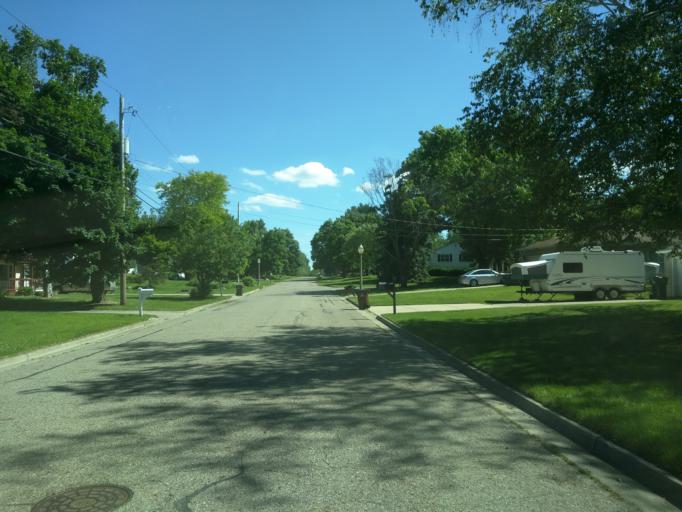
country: US
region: Michigan
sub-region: Ingham County
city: Edgemont Park
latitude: 42.7602
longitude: -84.5950
